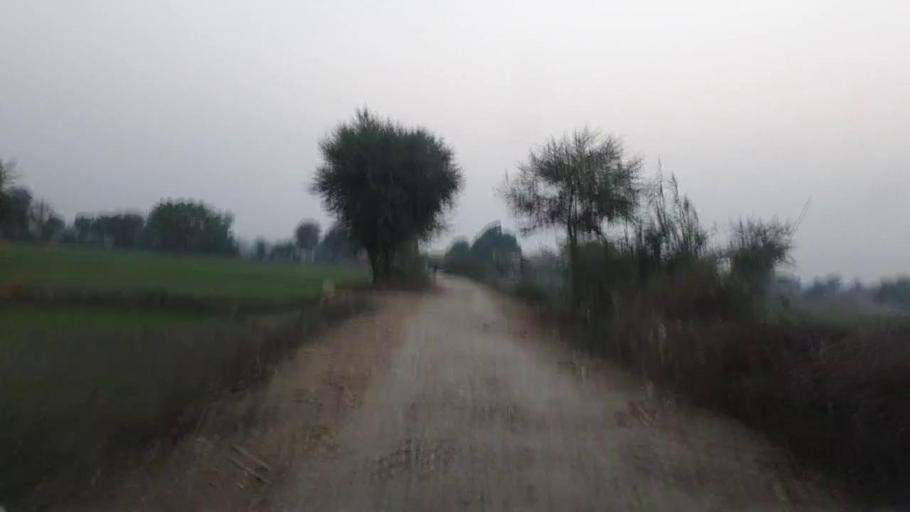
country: PK
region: Sindh
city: Karaundi
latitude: 26.9506
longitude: 68.4507
